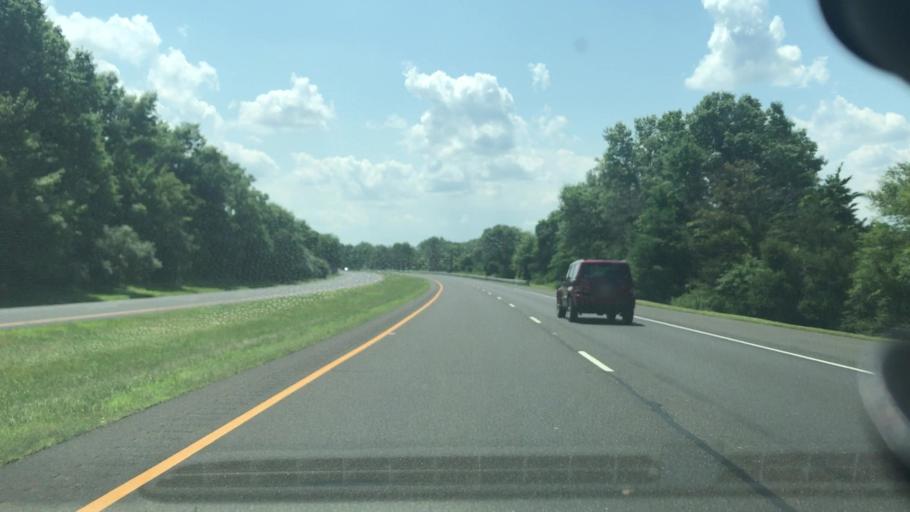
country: US
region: New Jersey
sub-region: Hunterdon County
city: Lambertville
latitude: 40.4162
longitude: -74.8863
